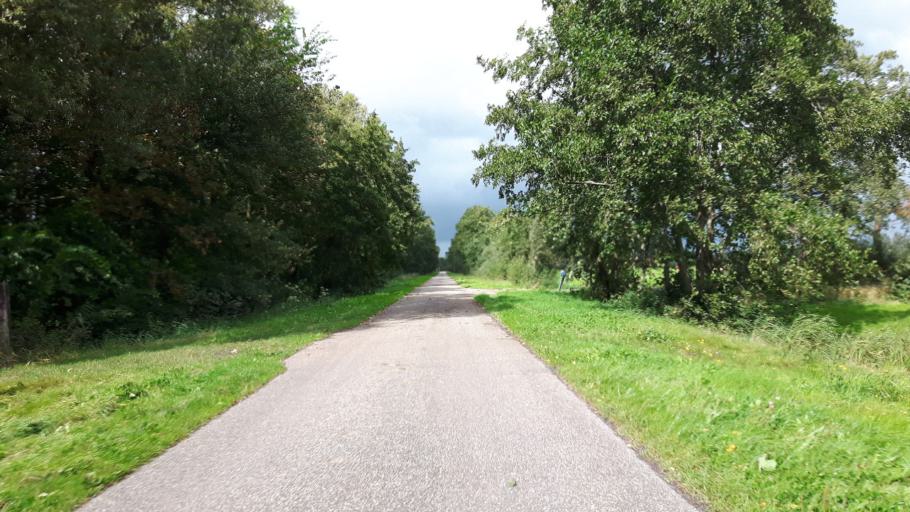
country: NL
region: Friesland
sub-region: Gemeente Dantumadiel
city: Broeksterwald
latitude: 53.2672
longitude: 5.9852
